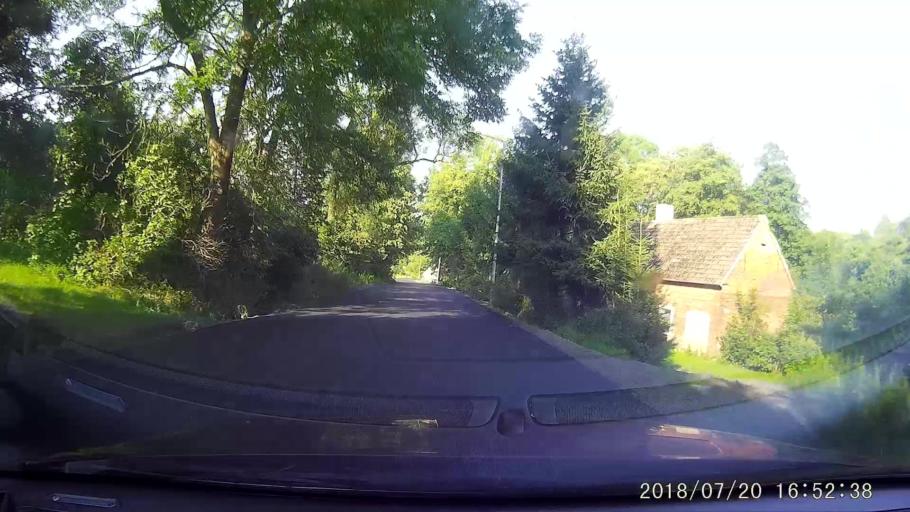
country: PL
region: Lower Silesian Voivodeship
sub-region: Powiat lubanski
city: Lesna
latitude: 51.0365
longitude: 15.2345
